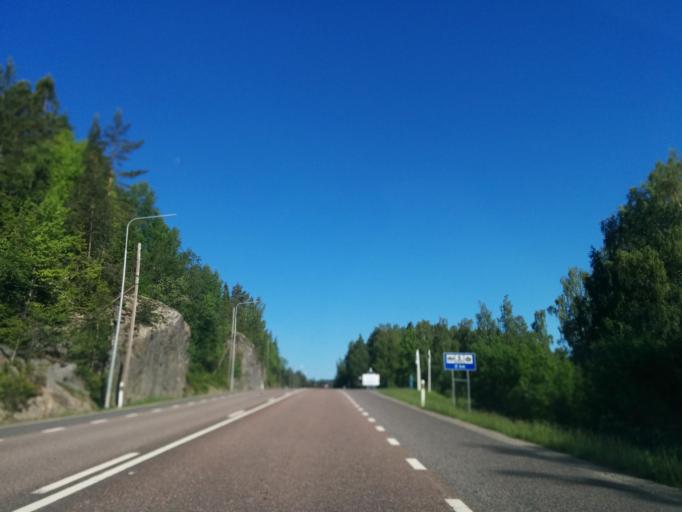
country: SE
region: Vaesternorrland
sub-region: Kramfors Kommun
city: Kramfors
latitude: 62.9107
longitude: 17.7949
